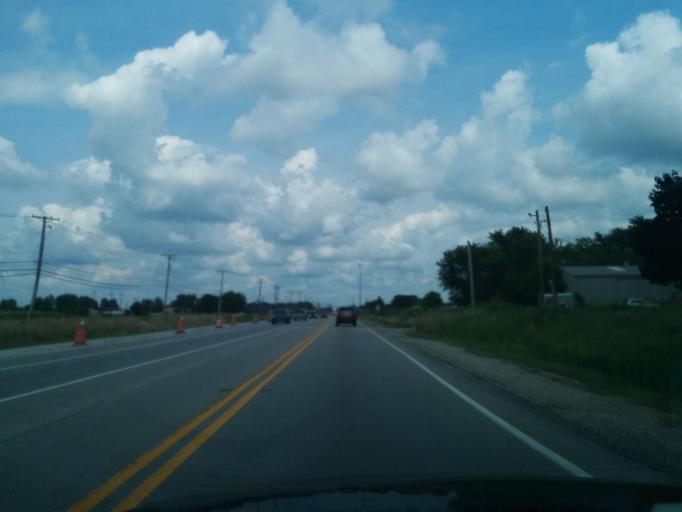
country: US
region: Illinois
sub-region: Will County
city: Homer Glen
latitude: 41.5994
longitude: -87.9572
